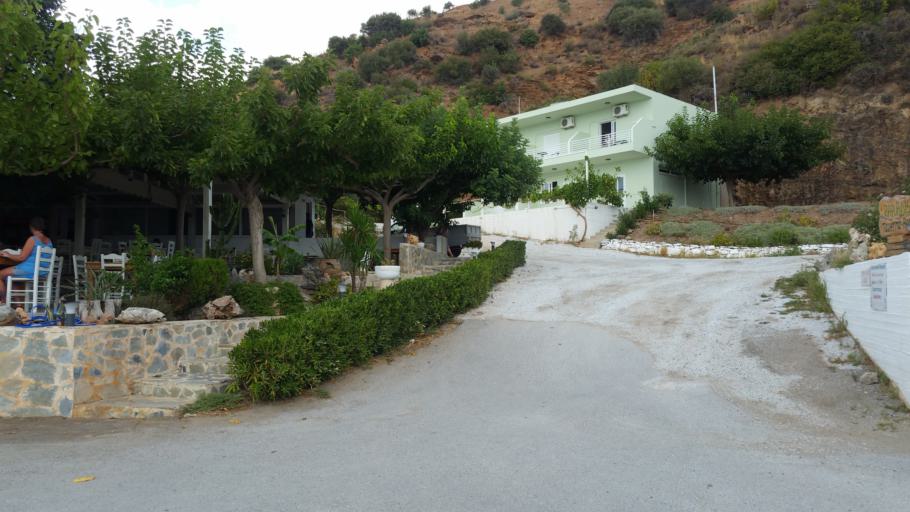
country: GR
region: Crete
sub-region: Nomos Chanias
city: Chora Sfakion
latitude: 35.1877
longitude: 24.3167
